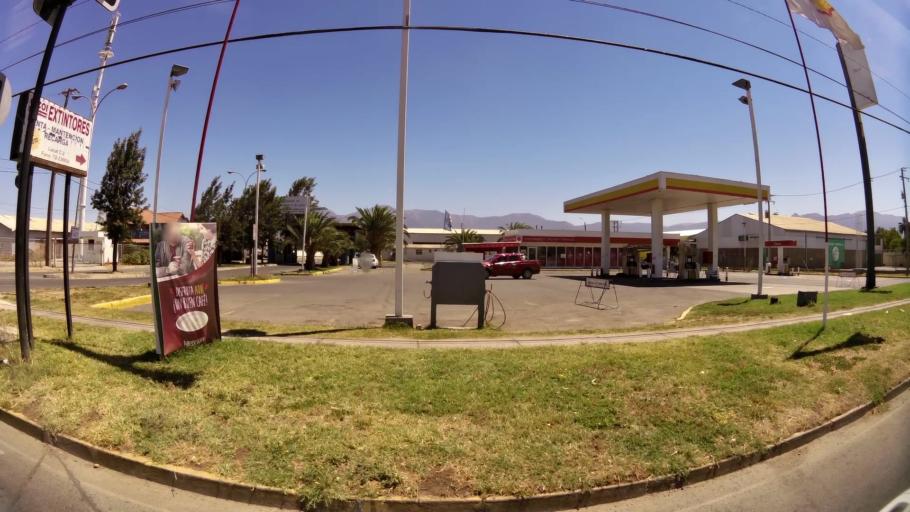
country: CL
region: O'Higgins
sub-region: Provincia de Cachapoal
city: Rancagua
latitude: -34.1542
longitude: -70.7679
